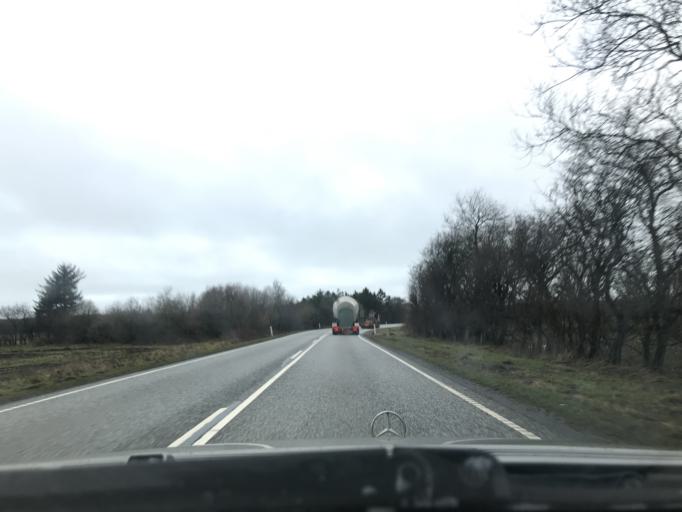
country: DK
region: South Denmark
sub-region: Haderslev Kommune
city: Gram
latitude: 55.2334
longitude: 8.9437
